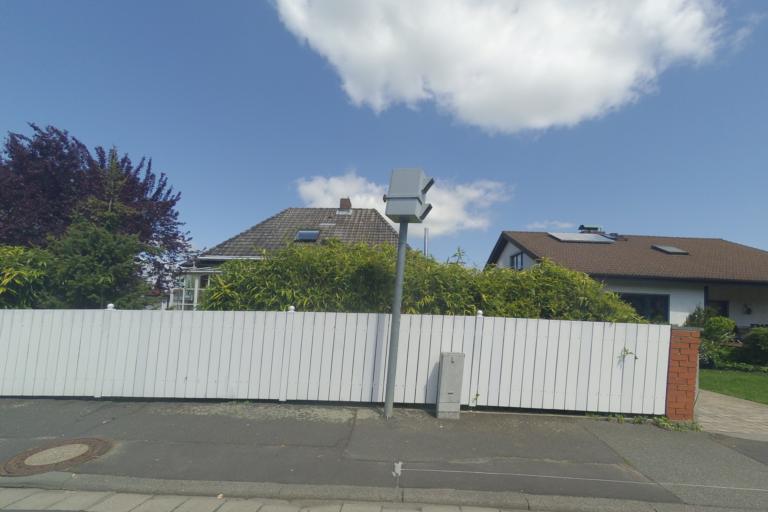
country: DE
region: Hesse
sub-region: Regierungsbezirk Darmstadt
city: Karben
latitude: 50.2418
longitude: 8.7223
